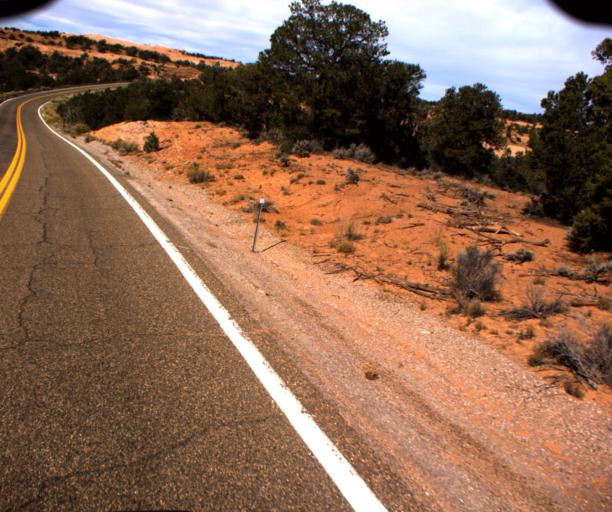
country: US
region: Arizona
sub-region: Navajo County
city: Kayenta
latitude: 36.6564
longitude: -110.5226
